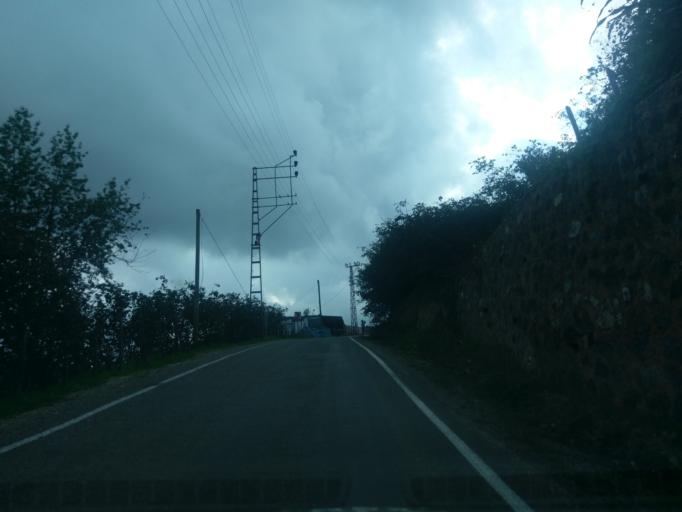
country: TR
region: Ordu
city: Camas
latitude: 40.8885
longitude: 37.6196
